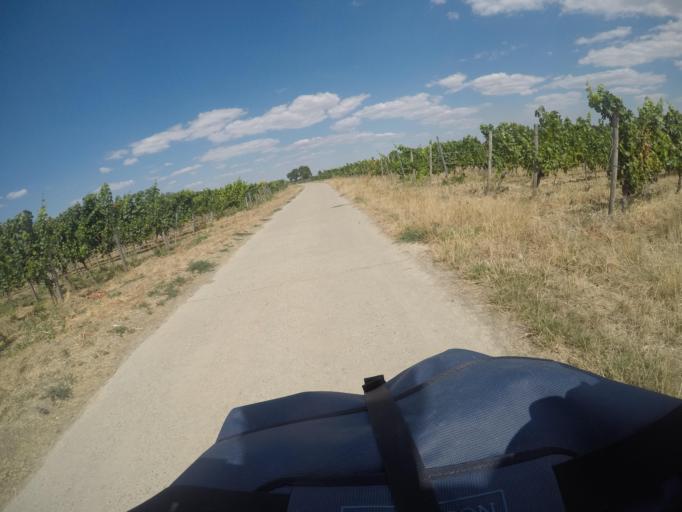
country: DE
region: Rheinland-Pfalz
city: Ludwigshohe
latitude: 49.8204
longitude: 8.3462
